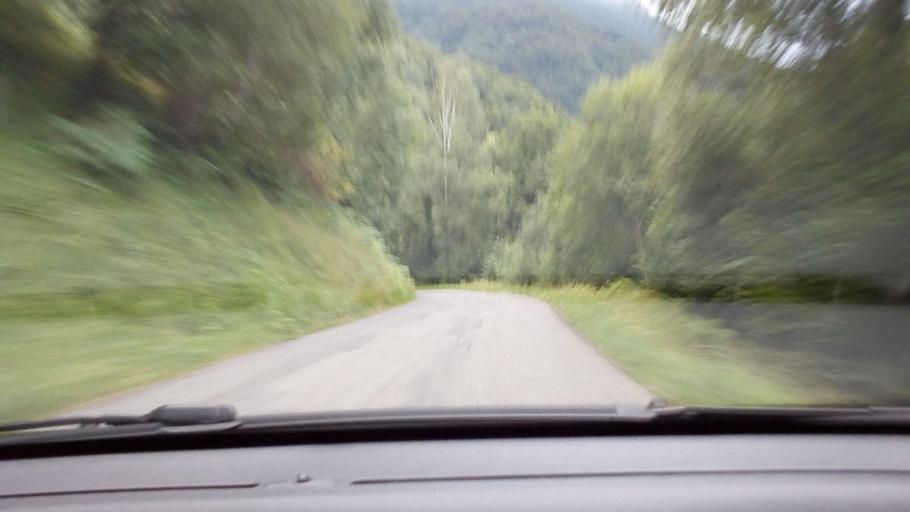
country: FR
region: Midi-Pyrenees
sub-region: Departement des Hautes-Pyrenees
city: Cauterets
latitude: 42.9470
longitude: -0.2134
